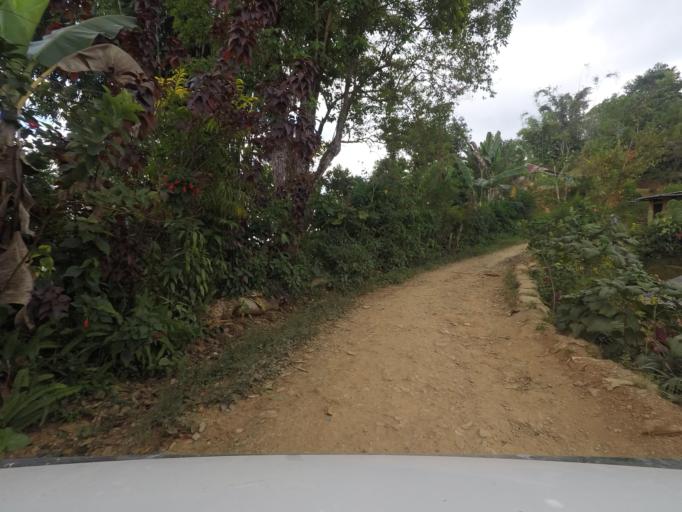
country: TL
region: Ermera
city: Gleno
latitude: -8.7216
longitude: 125.3249
